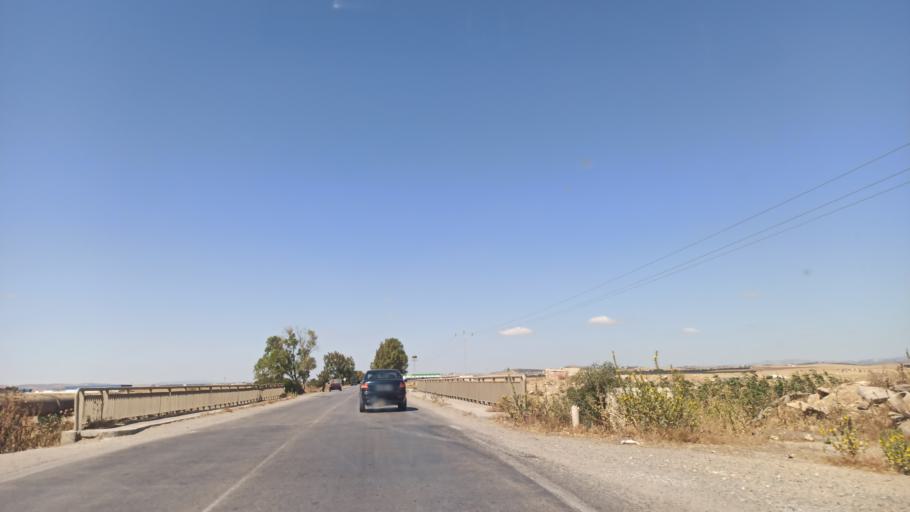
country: TN
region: Tunis
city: Oued Lill
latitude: 36.7438
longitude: 9.9612
